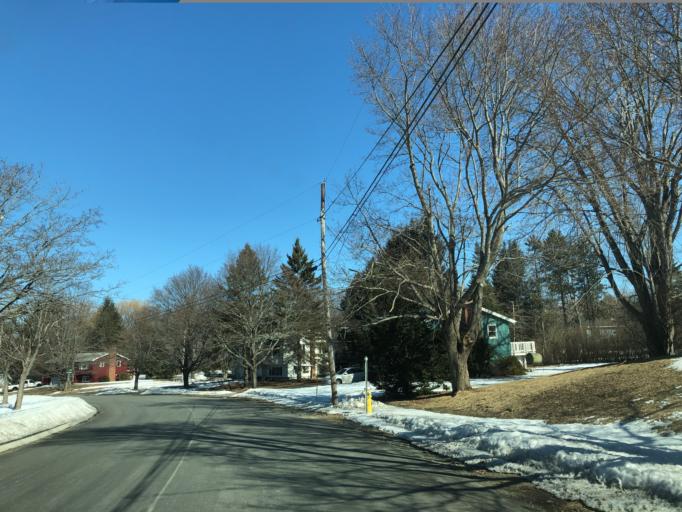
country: US
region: Maine
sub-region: Penobscot County
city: Brewer
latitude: 44.8200
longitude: -68.7565
